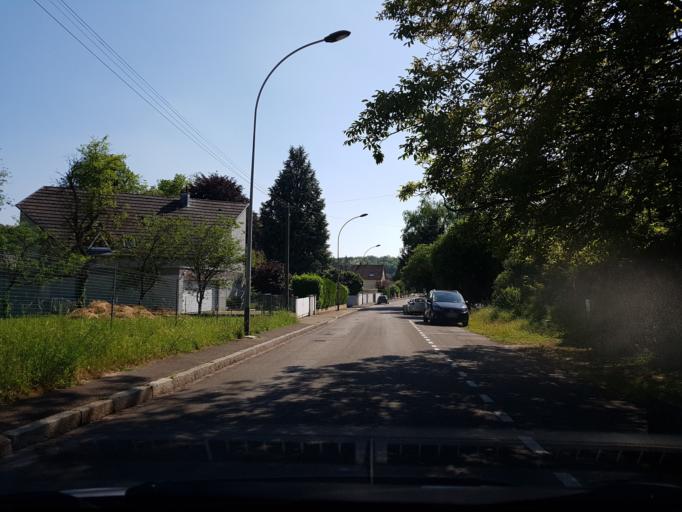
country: FR
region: Alsace
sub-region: Departement du Haut-Rhin
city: Riedisheim
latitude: 47.7391
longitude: 7.3646
